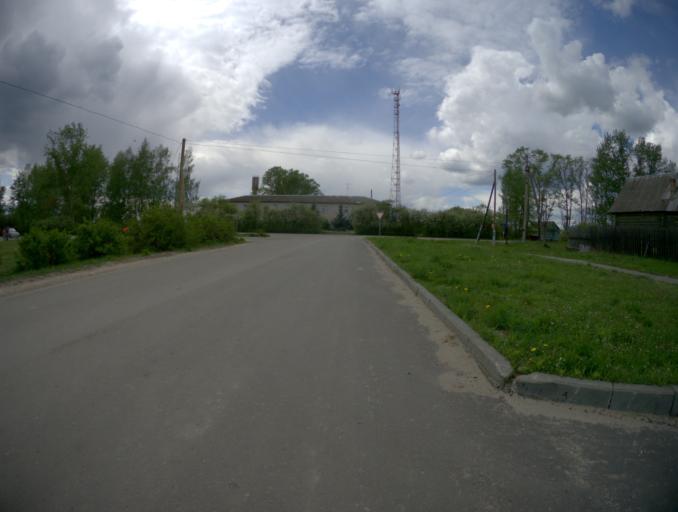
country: RU
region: Vladimir
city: Velikodvorskiy
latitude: 55.3345
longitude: 40.7527
